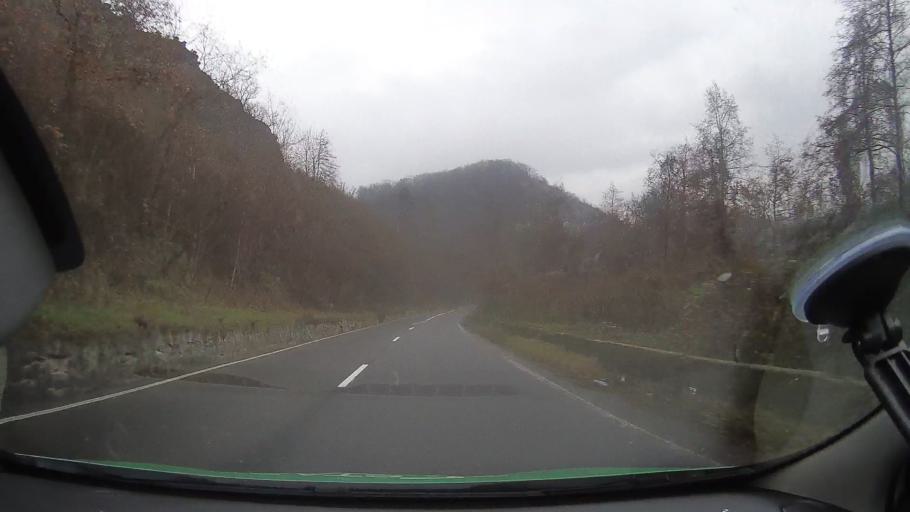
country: RO
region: Arad
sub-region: Comuna Gurahont
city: Gurahont
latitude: 46.2766
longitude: 22.3473
